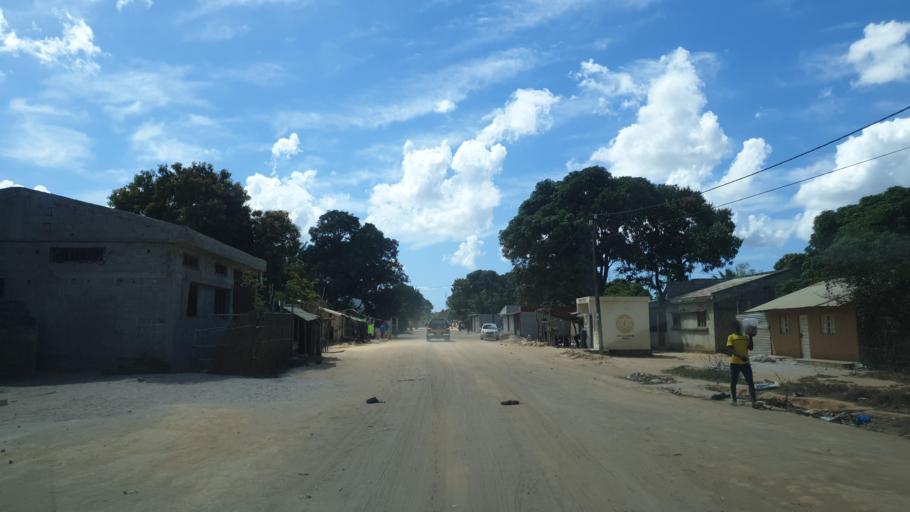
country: MZ
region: Nampula
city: Nacala
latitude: -14.5691
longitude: 40.6955
